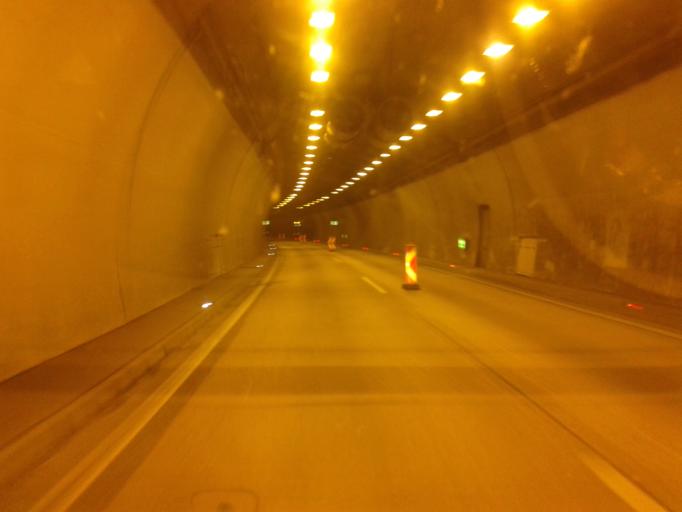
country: AT
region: Styria
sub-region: Politischer Bezirk Voitsberg
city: Modriach
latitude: 46.9716
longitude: 15.0832
